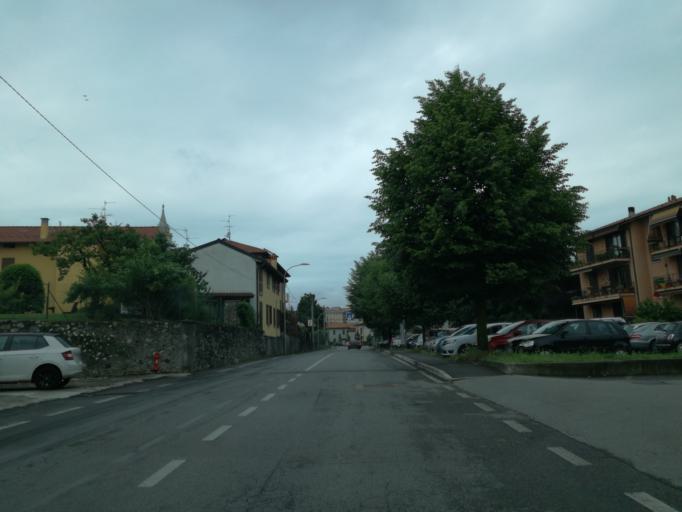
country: IT
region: Lombardy
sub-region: Provincia di Lecco
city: Robbiate
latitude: 45.6948
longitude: 9.4310
